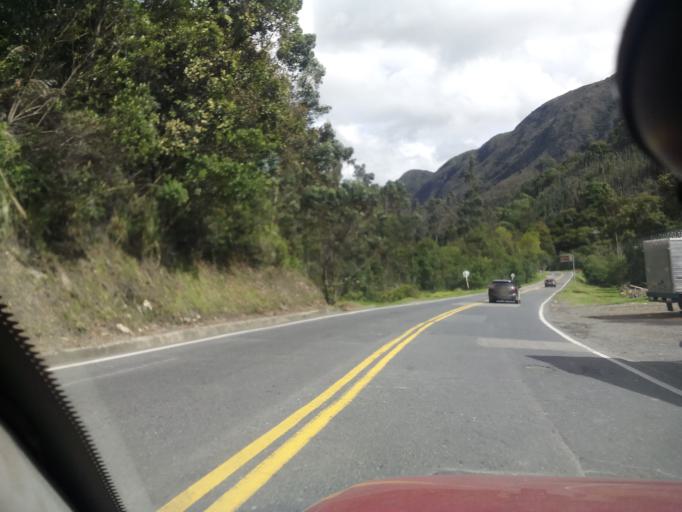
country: CO
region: Boyaca
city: Arcabuco
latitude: 5.7360
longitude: -73.4116
